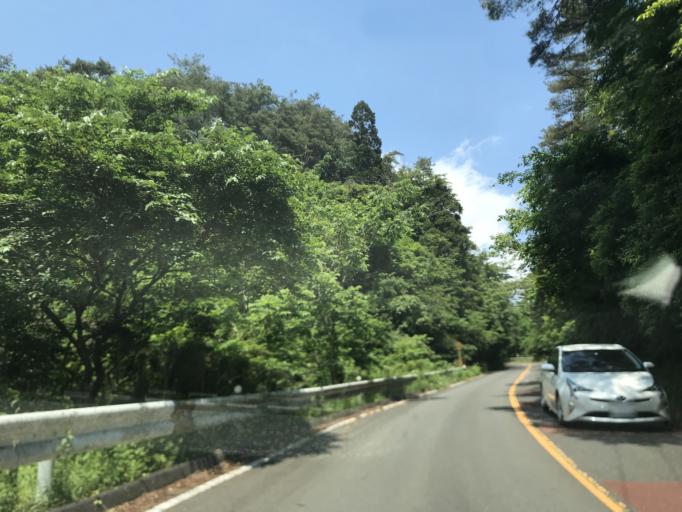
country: JP
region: Miyagi
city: Matsushima
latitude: 38.3564
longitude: 141.0573
